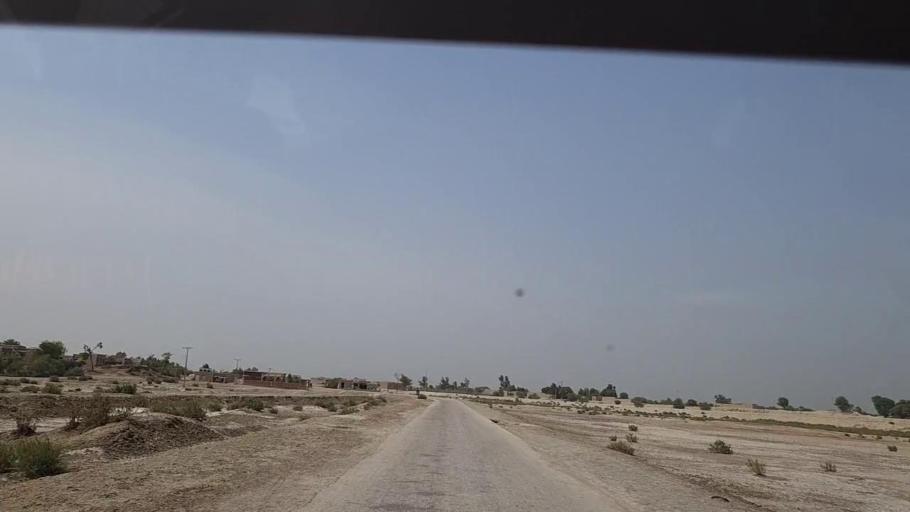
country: PK
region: Sindh
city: Khairpur Nathan Shah
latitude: 27.0713
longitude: 67.6513
